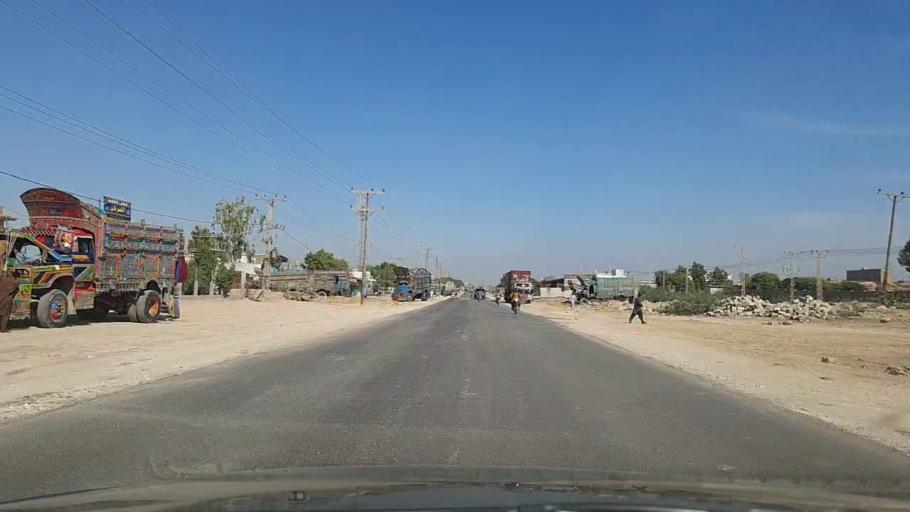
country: PK
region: Sindh
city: Kotri
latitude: 25.3459
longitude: 68.2598
